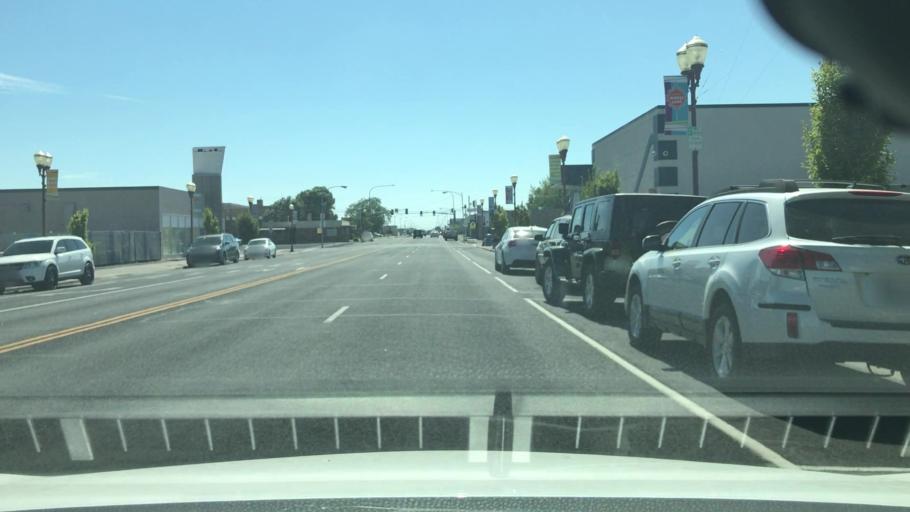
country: US
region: Washington
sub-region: Grant County
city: Moses Lake
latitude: 47.1289
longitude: -119.2808
